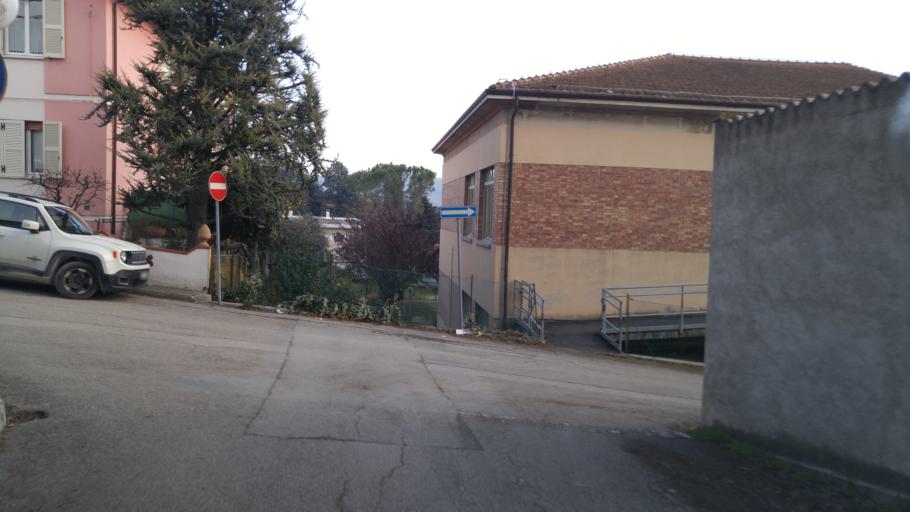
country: IT
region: The Marches
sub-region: Provincia di Pesaro e Urbino
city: Monte Porzio
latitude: 43.6903
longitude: 13.0458
